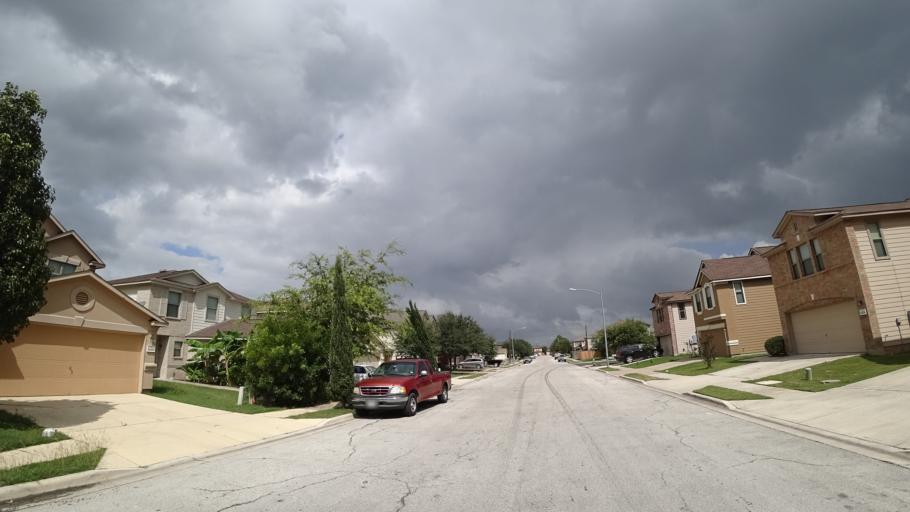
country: US
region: Texas
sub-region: Travis County
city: Onion Creek
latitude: 30.1505
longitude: -97.7430
